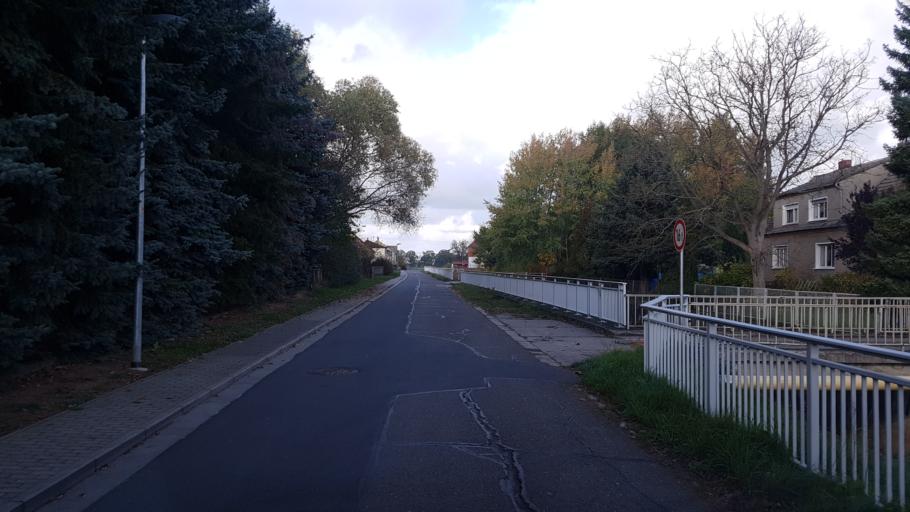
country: DE
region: Brandenburg
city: Doberlug-Kirchhain
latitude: 51.6389
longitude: 13.5559
